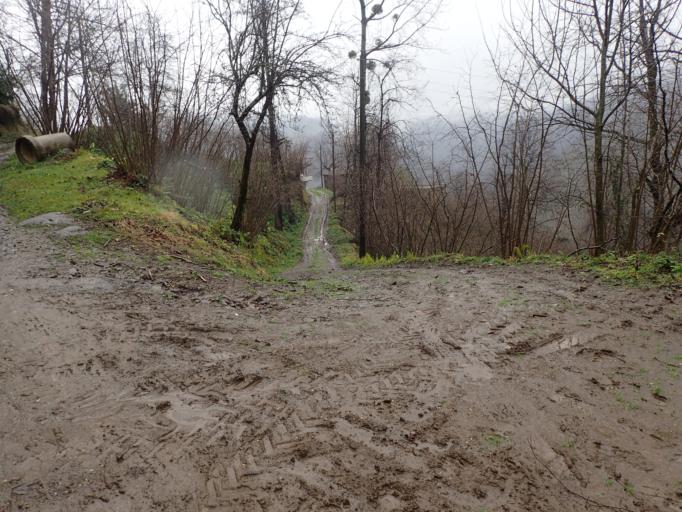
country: TR
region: Ordu
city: Camas
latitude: 40.9119
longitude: 37.5707
